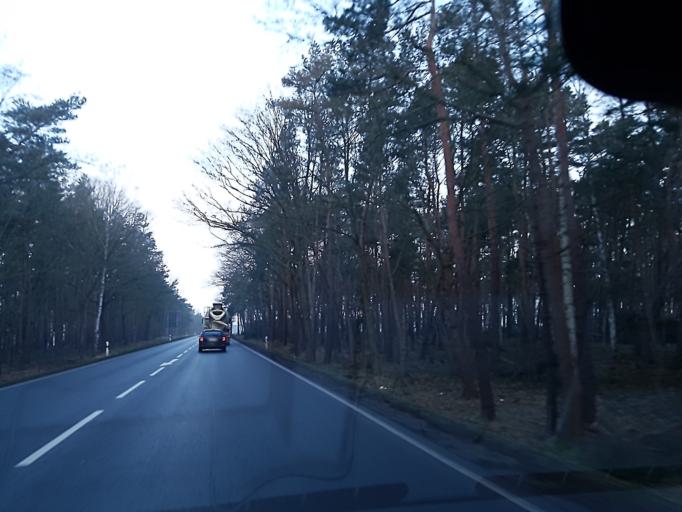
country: DE
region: Saxony-Anhalt
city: Elster
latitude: 51.8139
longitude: 12.8730
